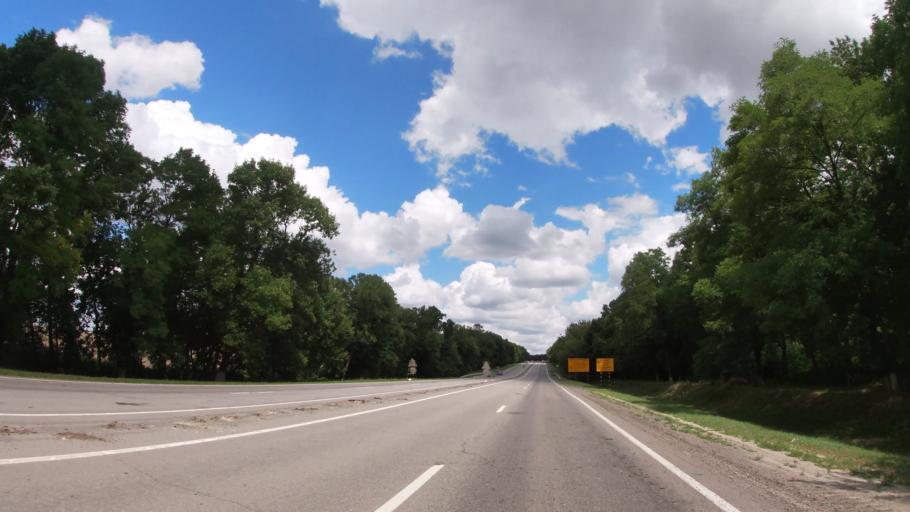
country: RU
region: Belgorod
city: Mayskiy
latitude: 50.4415
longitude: 36.3945
